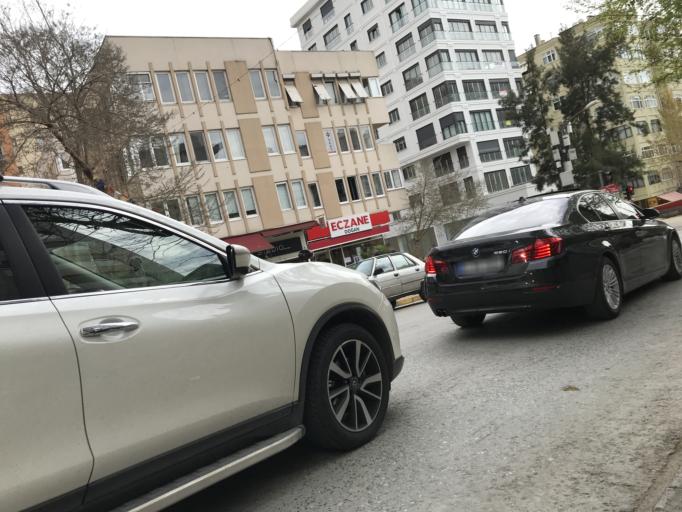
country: TR
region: Istanbul
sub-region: Atasehir
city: Atasehir
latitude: 40.9746
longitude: 29.0635
